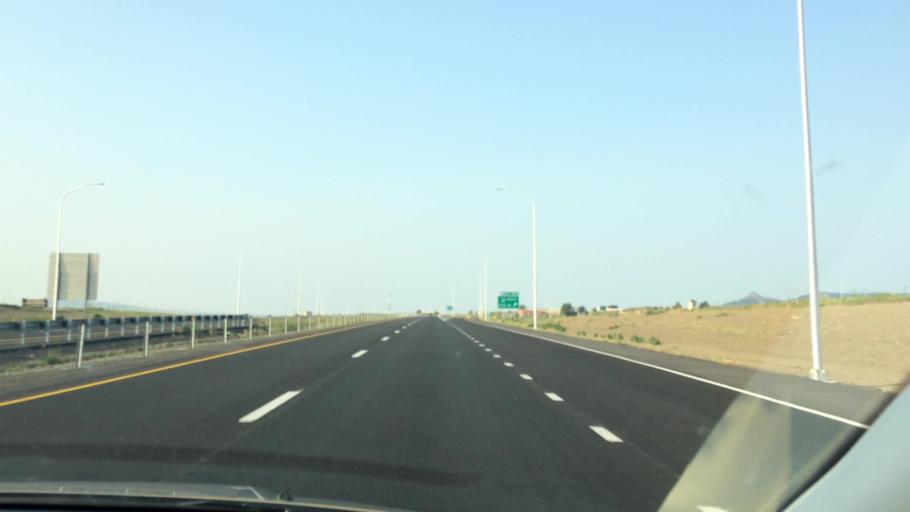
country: US
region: New Mexico
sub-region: Colfax County
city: Raton
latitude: 36.8698
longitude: -104.4373
